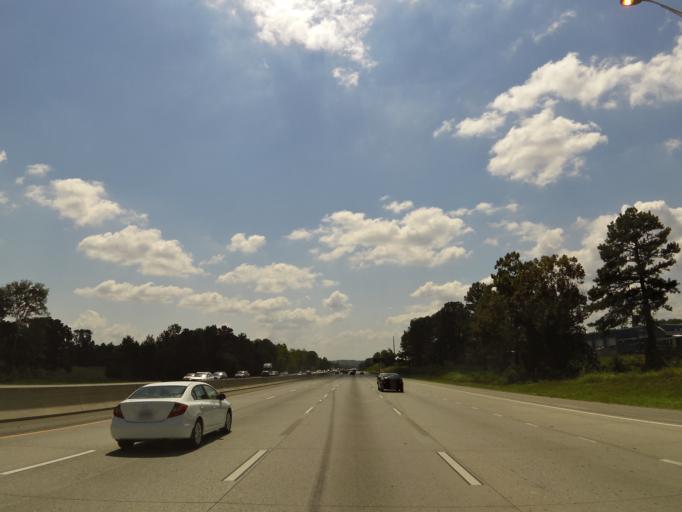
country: US
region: North Carolina
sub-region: Cabarrus County
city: Harrisburg
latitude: 35.3975
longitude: -80.7004
